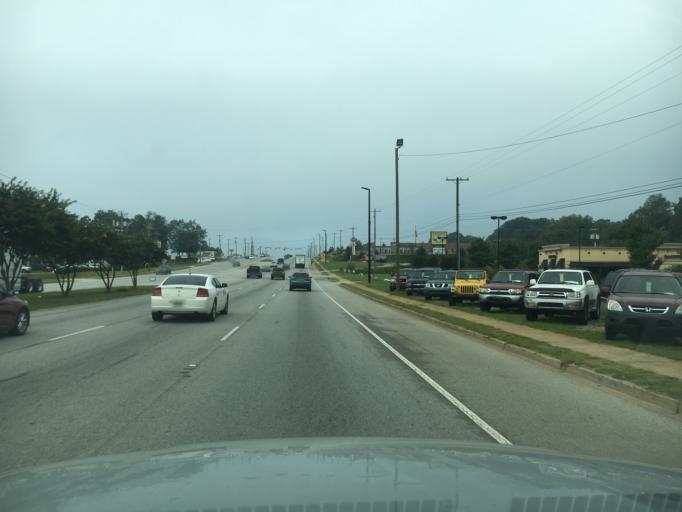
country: US
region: South Carolina
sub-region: Greenville County
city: Greer
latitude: 34.9453
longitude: -82.2499
